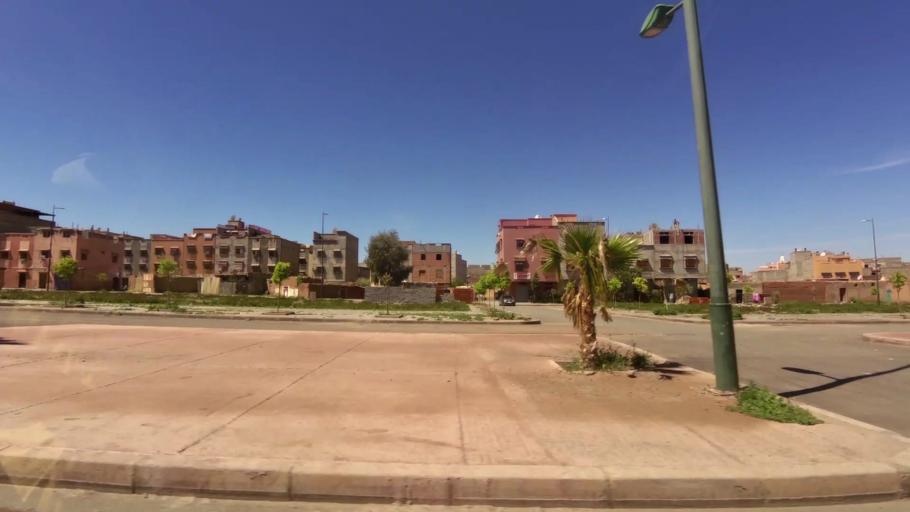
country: MA
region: Marrakech-Tensift-Al Haouz
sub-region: Marrakech
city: Marrakesh
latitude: 31.5611
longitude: -7.9783
